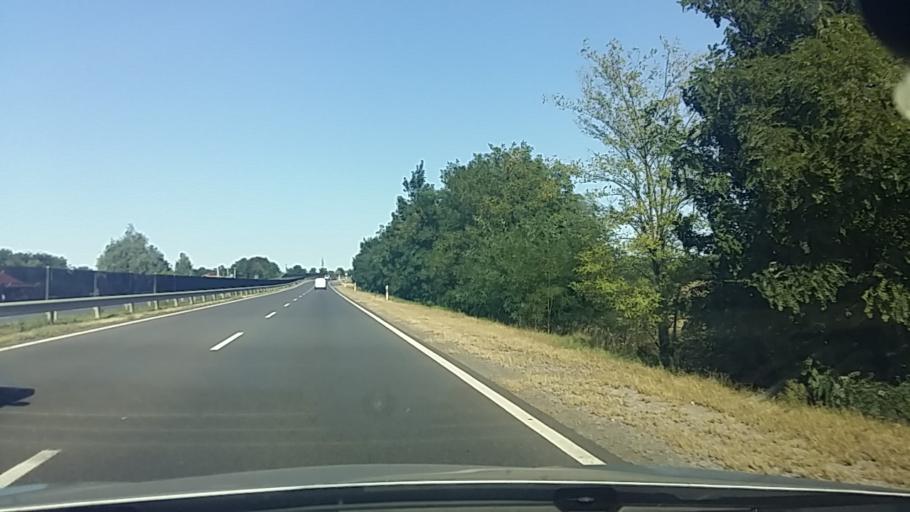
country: HU
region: Szabolcs-Szatmar-Bereg
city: Nyiregyhaza
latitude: 47.9074
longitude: 21.7133
